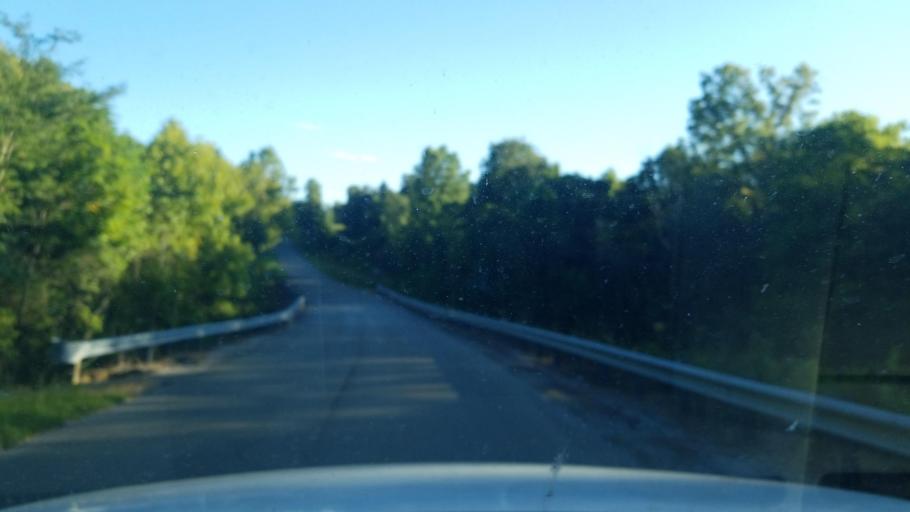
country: US
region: Illinois
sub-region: Hardin County
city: Elizabethtown
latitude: 37.5908
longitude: -88.3656
